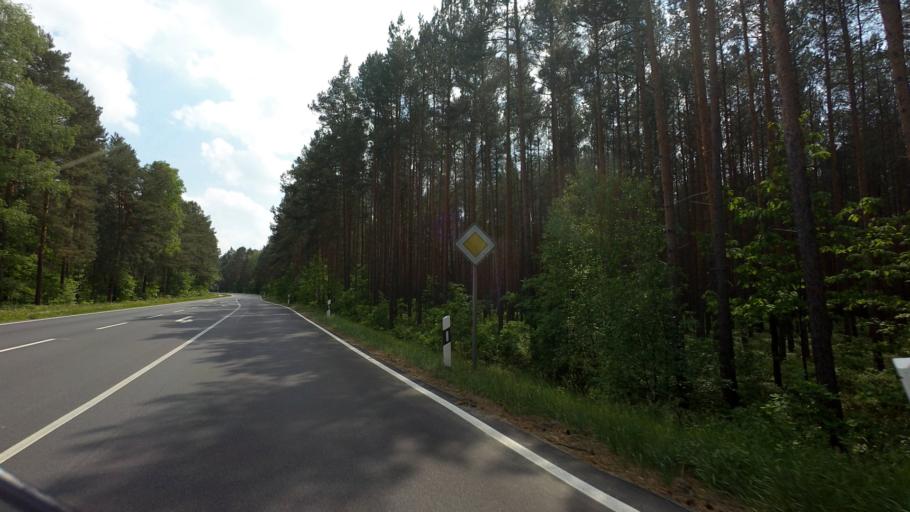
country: DE
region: Saxony
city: Rietschen
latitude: 51.3471
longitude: 14.8040
